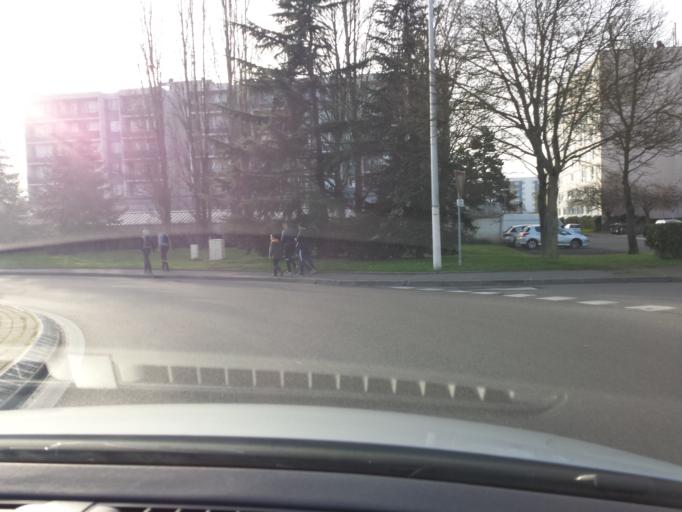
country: FR
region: Haute-Normandie
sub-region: Departement de l'Eure
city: Evreux
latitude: 49.0098
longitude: 1.1668
